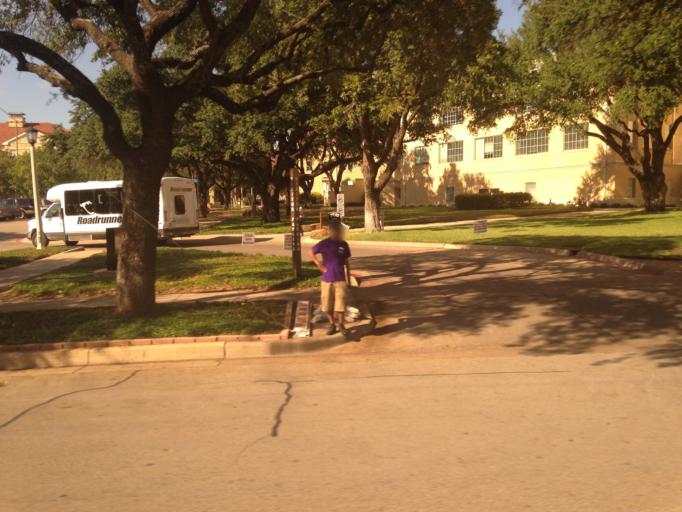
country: US
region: Texas
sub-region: Tarrant County
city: Fort Worth
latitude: 32.7070
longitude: -97.3618
